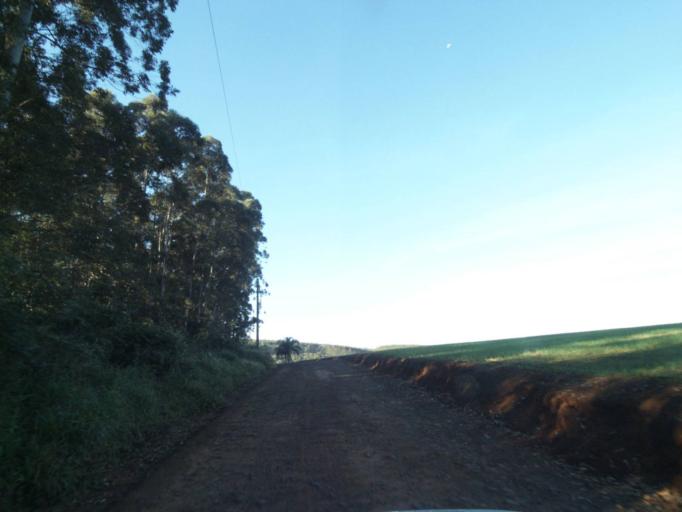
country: BR
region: Parana
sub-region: Telemaco Borba
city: Telemaco Borba
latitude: -24.4782
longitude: -50.5884
